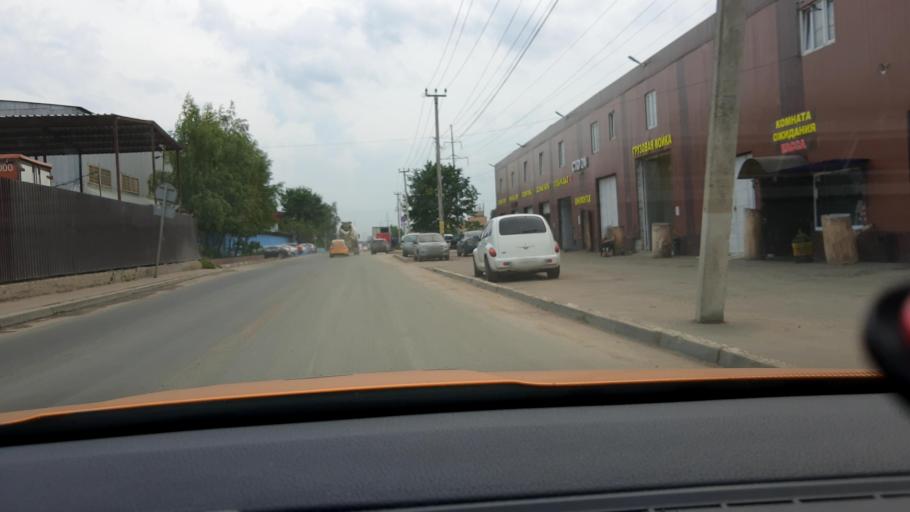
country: RU
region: Moskovskaya
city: Mosrentgen
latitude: 55.6210
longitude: 37.4640
